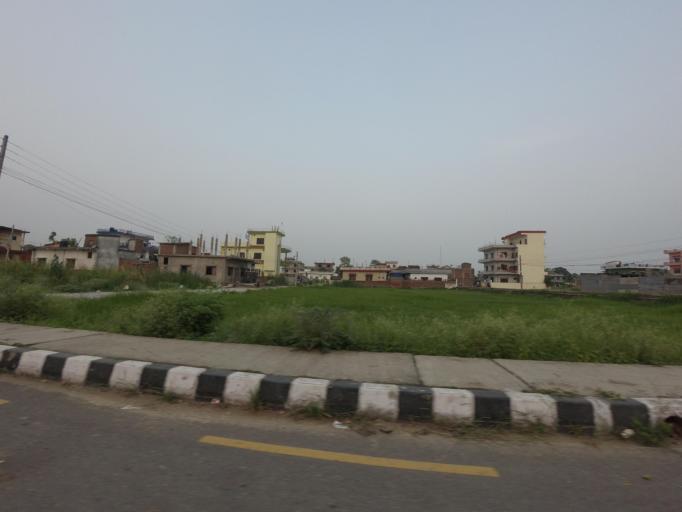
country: NP
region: Western Region
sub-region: Lumbini Zone
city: Bhairahawa
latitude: 27.5026
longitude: 83.4607
